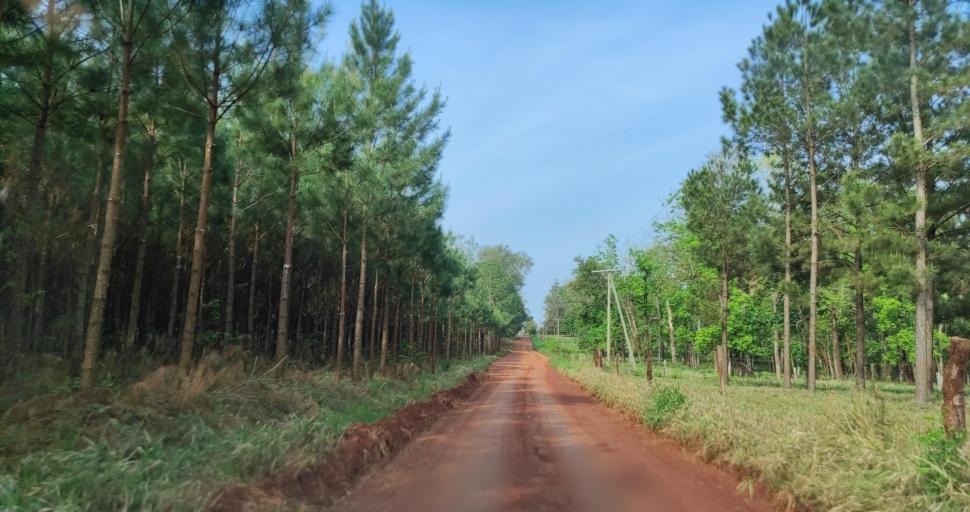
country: AR
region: Misiones
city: Garuhape
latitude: -26.8663
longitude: -54.9987
